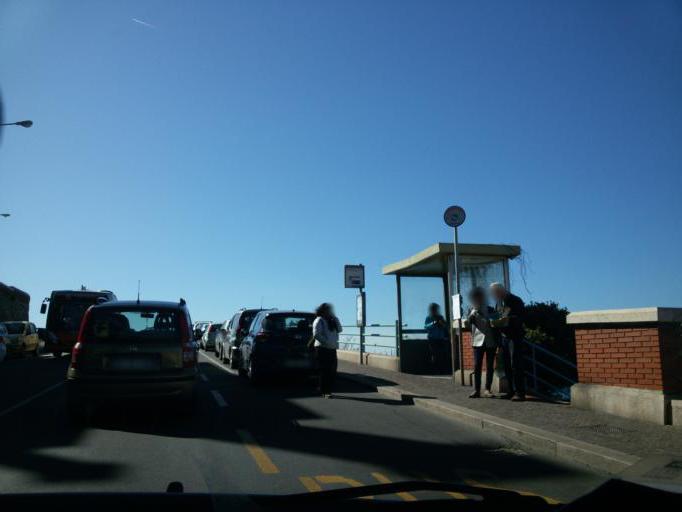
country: IT
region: Liguria
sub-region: Provincia di Genova
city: Bogliasco
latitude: 44.3869
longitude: 8.9980
